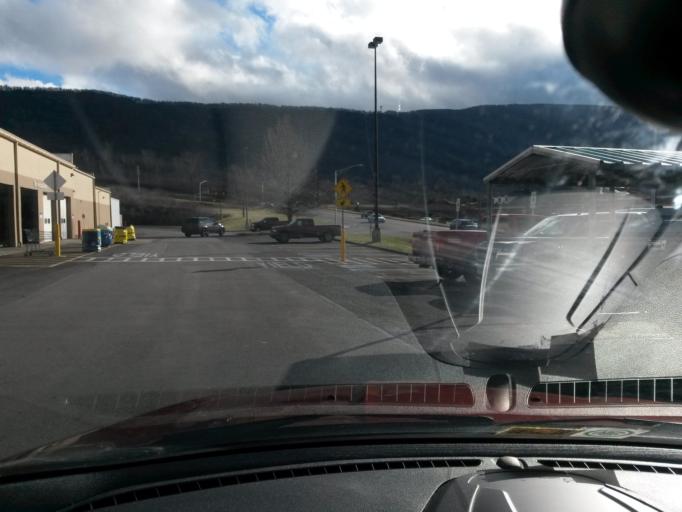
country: US
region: Virginia
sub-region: Tazewell County
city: Bluefield
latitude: 37.2399
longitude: -81.2491
